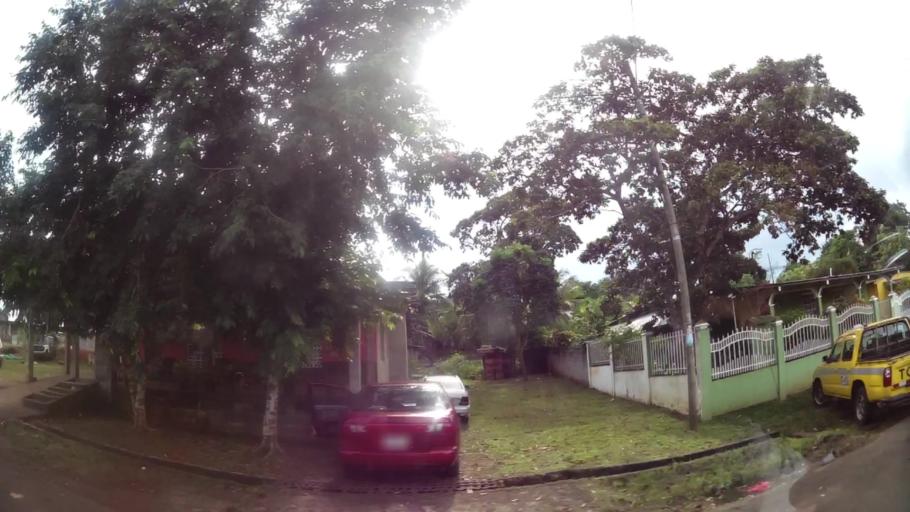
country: PA
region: Panama
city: El Coco
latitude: 8.8784
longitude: -79.8097
